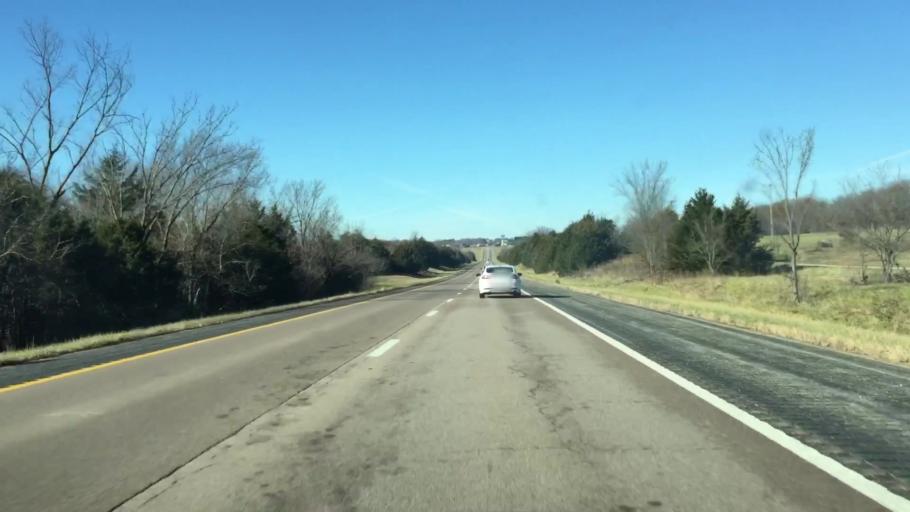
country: US
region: Missouri
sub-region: Miller County
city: Eldon
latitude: 38.3677
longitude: -92.4848
